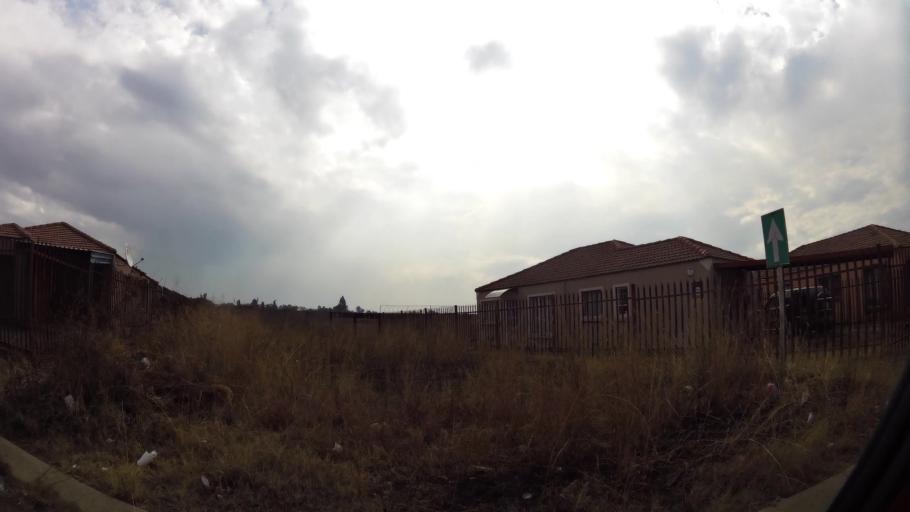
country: ZA
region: Gauteng
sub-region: Sedibeng District Municipality
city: Vanderbijlpark
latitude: -26.7145
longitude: 27.8865
